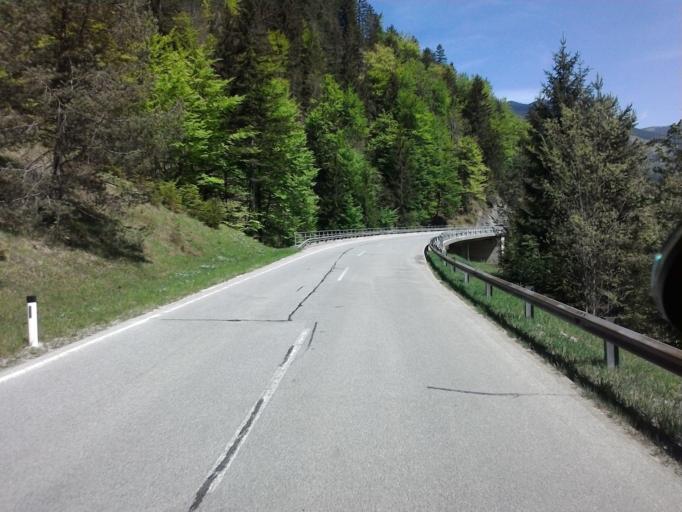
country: AT
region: Styria
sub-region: Politischer Bezirk Liezen
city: Gams bei Hieflau
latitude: 47.6894
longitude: 14.7762
